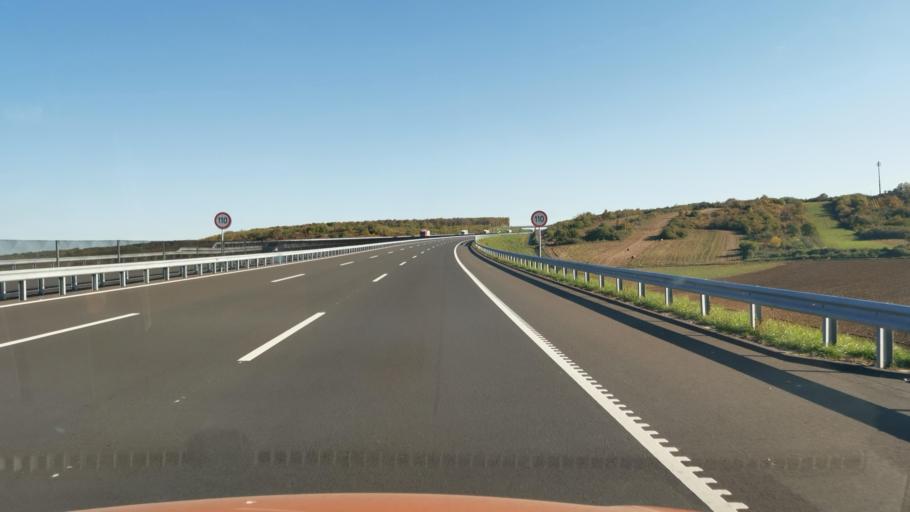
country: HU
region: Borsod-Abauj-Zemplen
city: Szikszo
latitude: 48.2102
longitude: 20.9171
